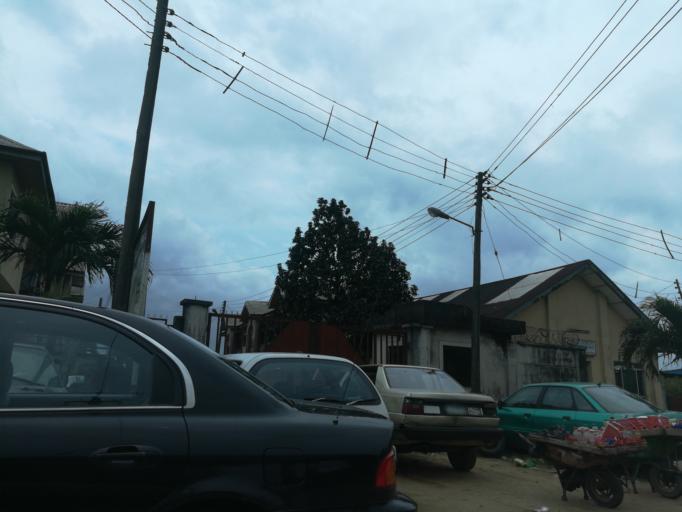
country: NG
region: Rivers
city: Port Harcourt
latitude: 4.7649
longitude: 7.0256
